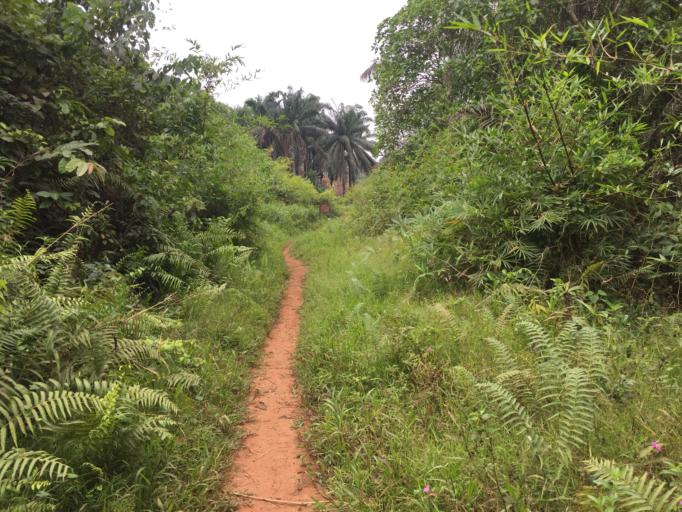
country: NG
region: Imo
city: Ihuo
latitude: 5.4635
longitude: 7.1485
